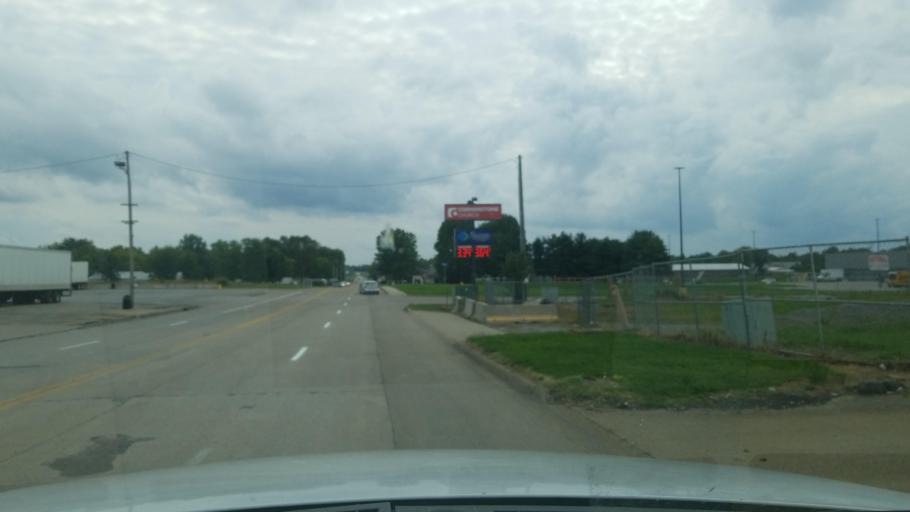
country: US
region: Illinois
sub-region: Williamson County
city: Marion
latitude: 37.7402
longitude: -88.9655
